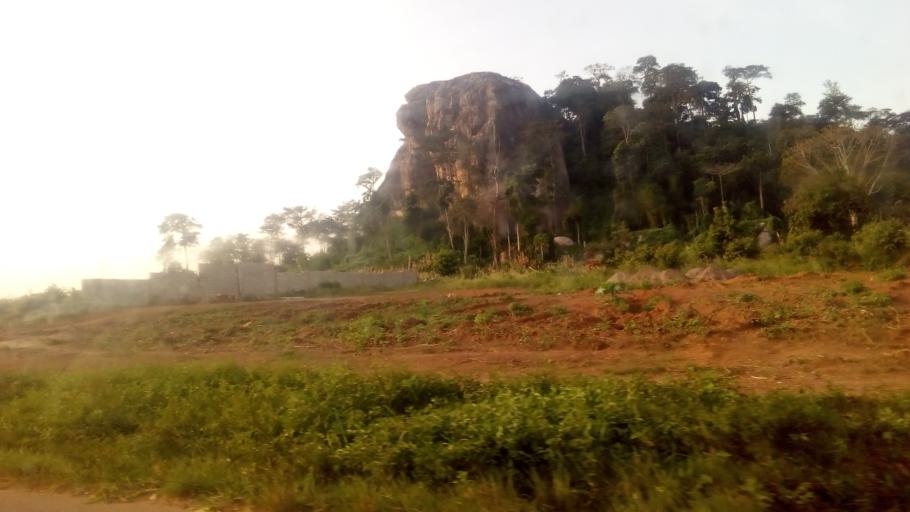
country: CI
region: Dix-Huit Montagnes
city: Duekoue
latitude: 6.7522
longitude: -7.3666
